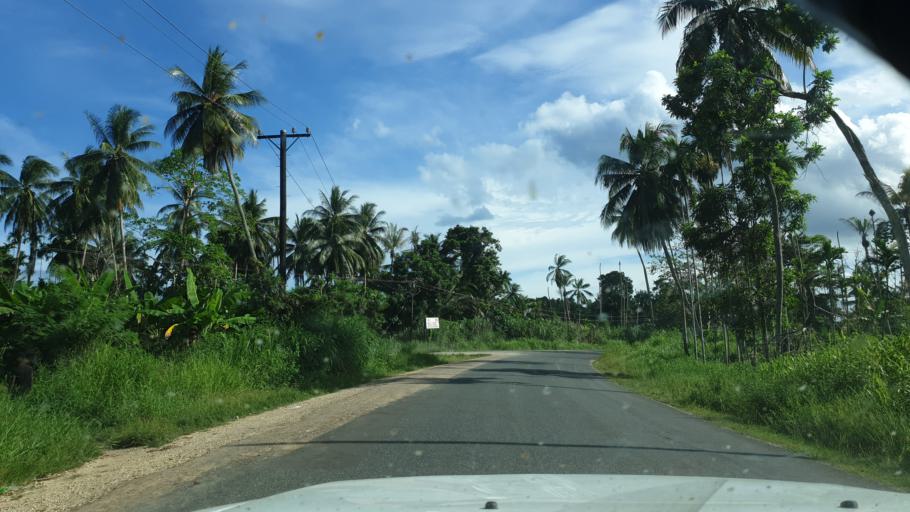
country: PG
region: Madang
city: Madang
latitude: -5.0964
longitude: 145.7948
